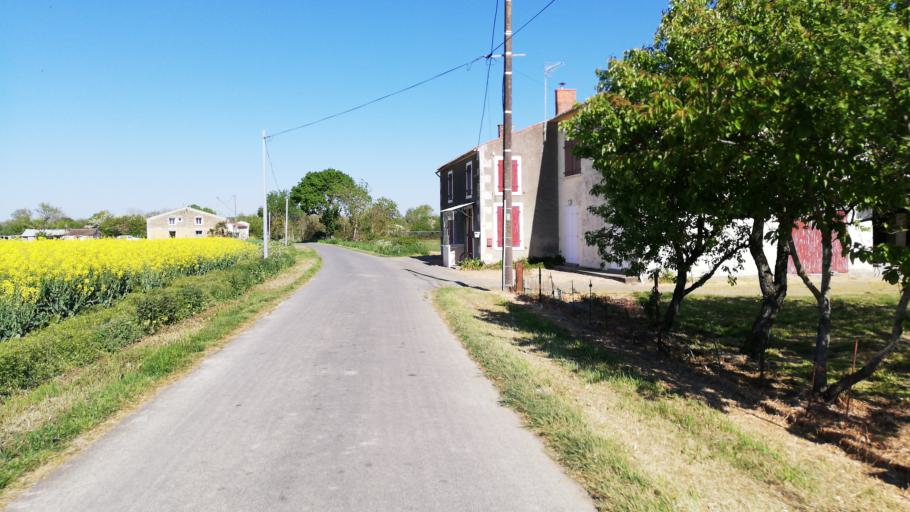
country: FR
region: Pays de la Loire
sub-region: Departement de la Vendee
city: Maillezais
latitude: 46.3267
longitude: -0.7469
